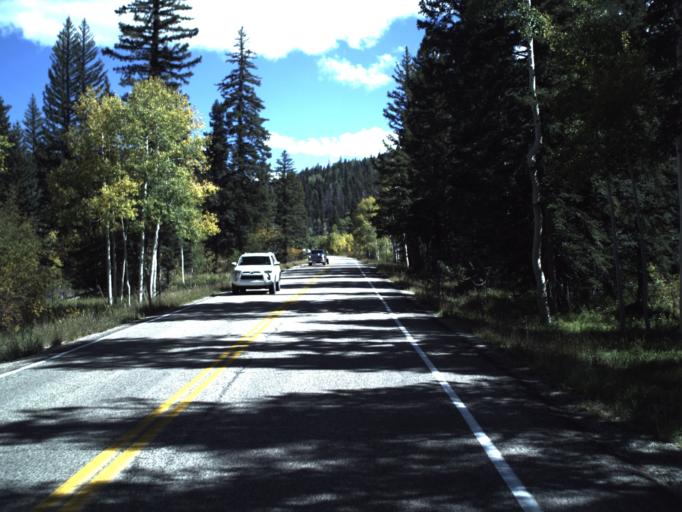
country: US
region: Utah
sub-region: Iron County
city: Cedar City
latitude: 37.5956
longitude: -112.9225
